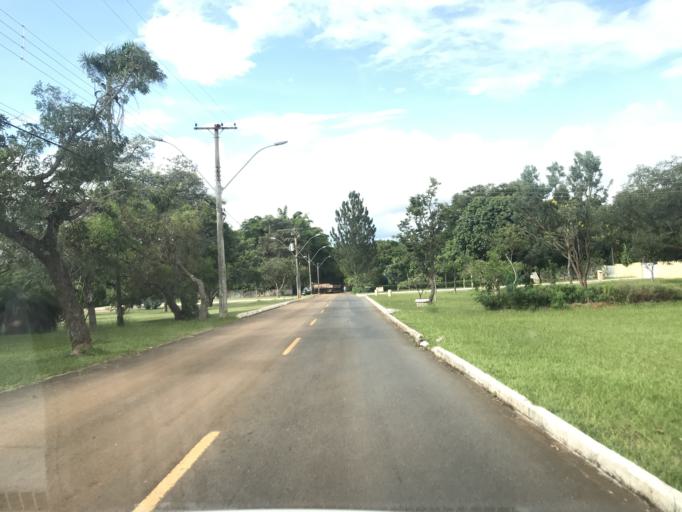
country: BR
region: Federal District
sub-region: Brasilia
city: Brasilia
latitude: -15.8858
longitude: -47.9172
